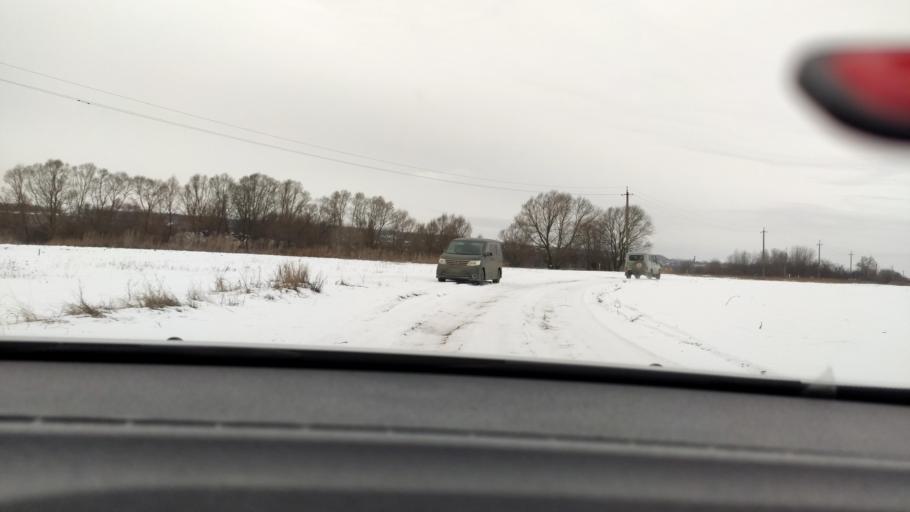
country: RU
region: Voronezj
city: Semiluki
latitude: 51.7026
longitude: 38.9715
